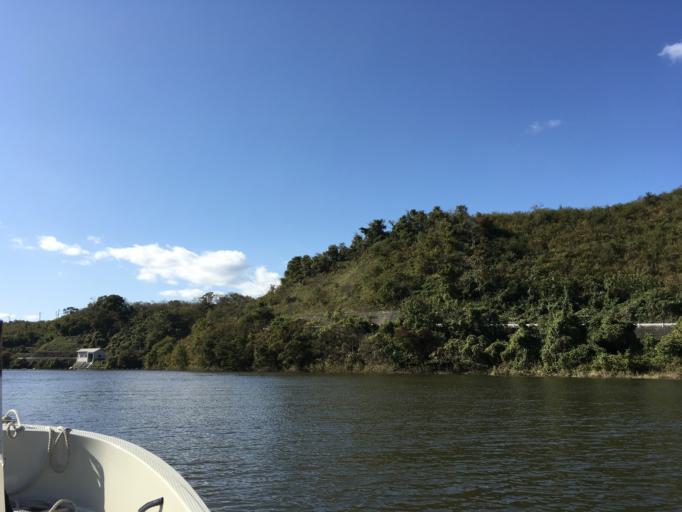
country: JP
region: Iwate
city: Ichinoseki
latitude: 38.7987
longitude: 141.2875
